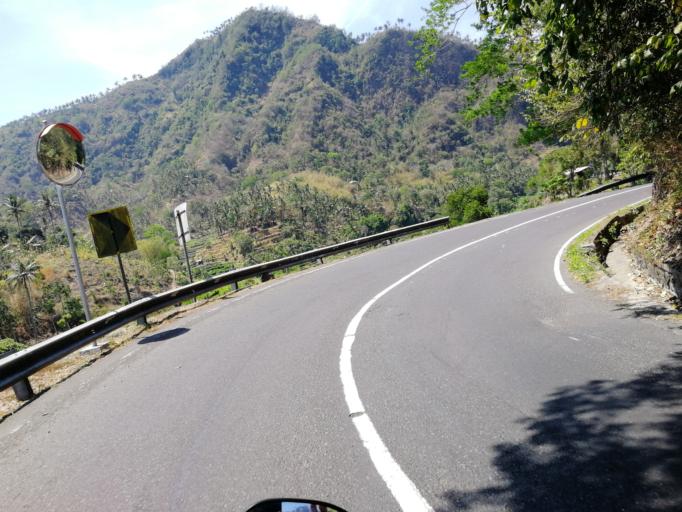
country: ID
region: Bali
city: Tistagede
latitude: -8.3702
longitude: 115.6093
